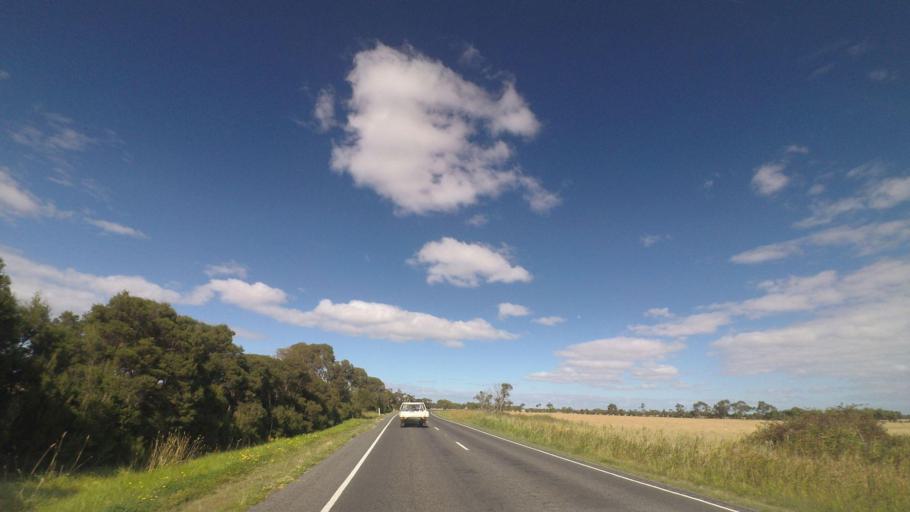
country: AU
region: Victoria
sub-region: Cardinia
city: Koo-Wee-Rup
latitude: -38.1847
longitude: 145.5473
